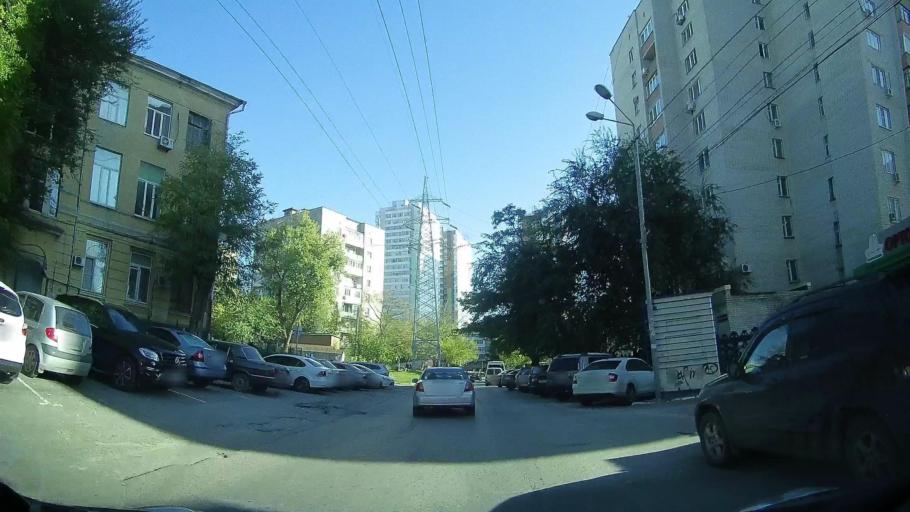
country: RU
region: Rostov
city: Rostov-na-Donu
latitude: 47.2247
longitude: 39.6930
